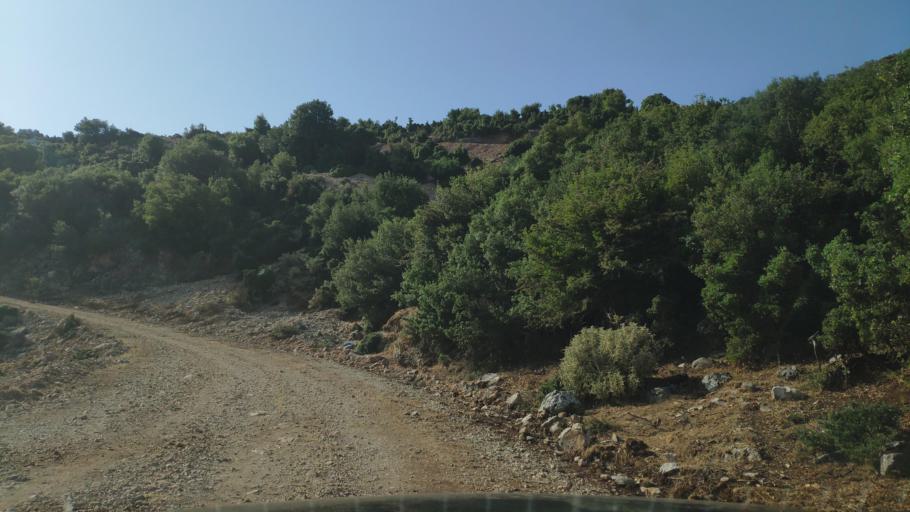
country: GR
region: West Greece
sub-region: Nomos Aitolias kai Akarnanias
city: Monastirakion
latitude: 38.8349
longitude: 20.9815
